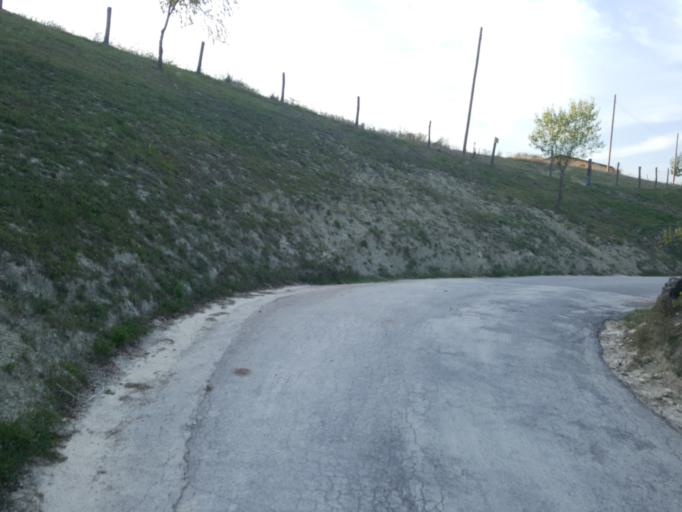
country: IT
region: The Marches
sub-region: Provincia di Ancona
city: Fabriano
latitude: 43.3492
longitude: 12.8412
